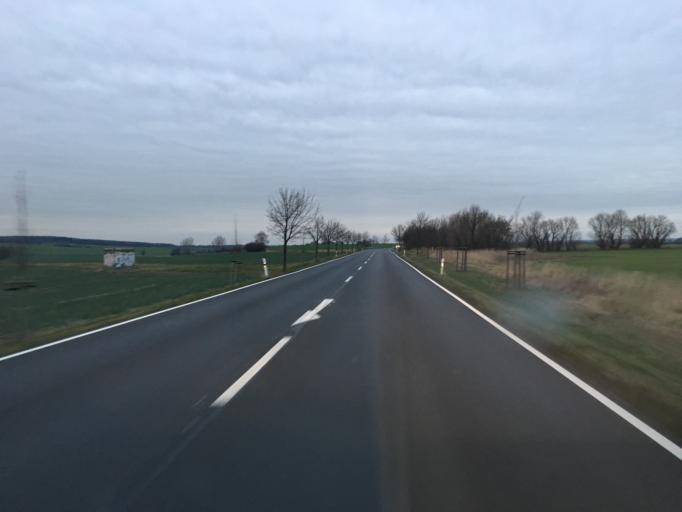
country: DE
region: Saxony
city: Oschatz
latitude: 51.3063
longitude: 13.0904
